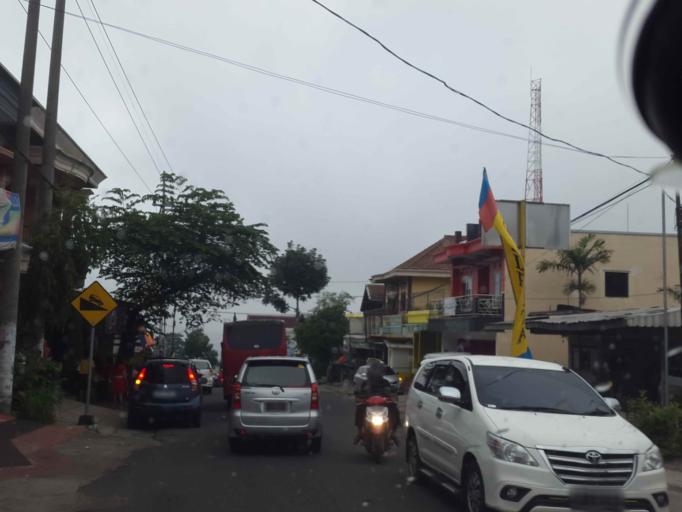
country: ID
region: East Java
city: Batu
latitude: -7.8250
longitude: 112.5298
